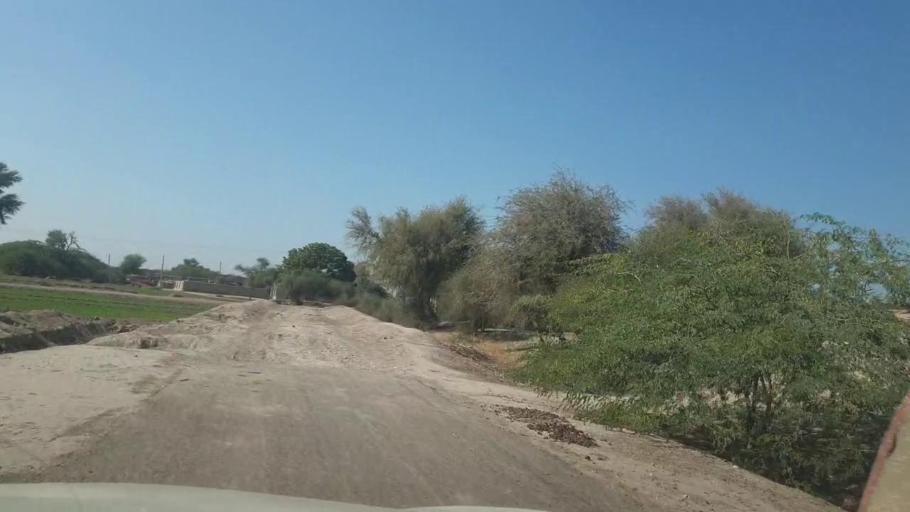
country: PK
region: Sindh
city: Bhan
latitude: 26.5664
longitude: 67.6882
